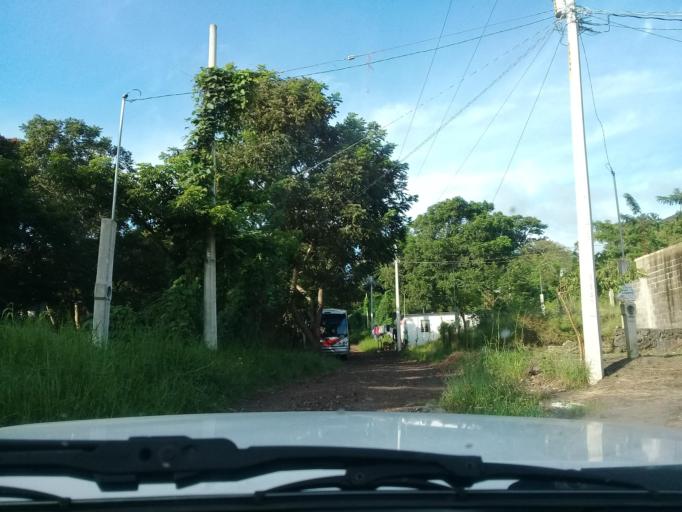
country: MX
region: Veracruz
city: Catemaco
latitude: 18.4326
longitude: -95.1084
